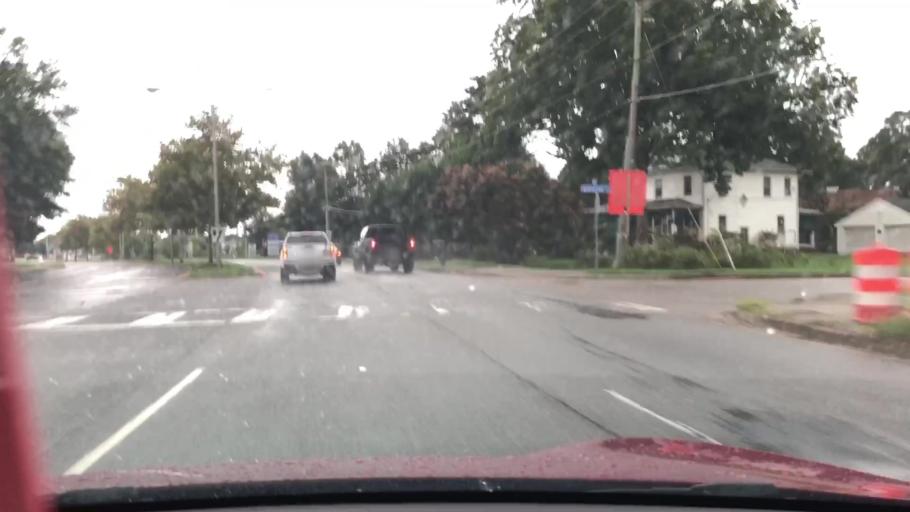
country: US
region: Virginia
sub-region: City of Chesapeake
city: Chesapeake
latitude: 36.8442
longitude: -76.1903
